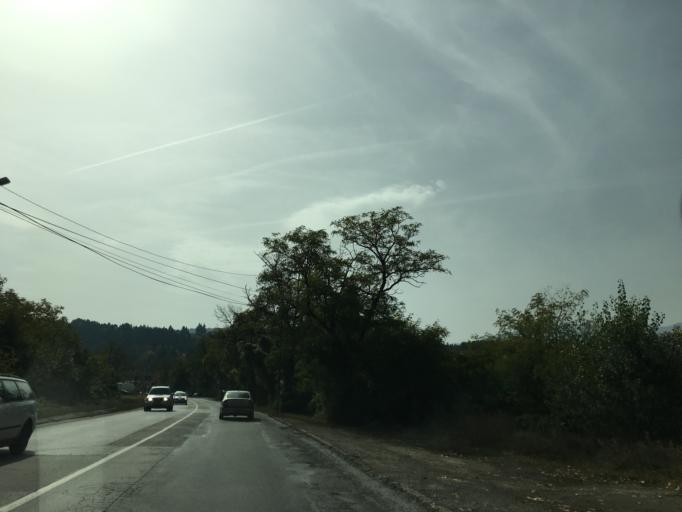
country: BG
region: Sofia-Capital
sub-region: Stolichna Obshtina
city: Sofia
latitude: 42.6131
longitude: 23.3998
